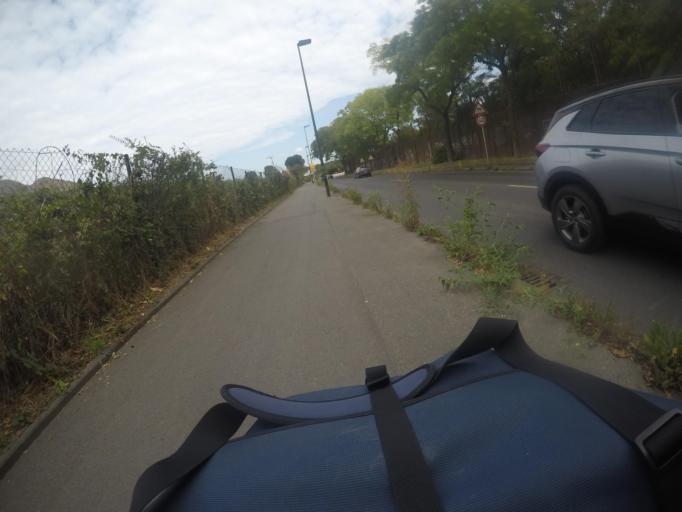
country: DE
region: North Rhine-Westphalia
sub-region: Regierungsbezirk Dusseldorf
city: Erkrath
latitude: 51.2216
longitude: 6.8497
